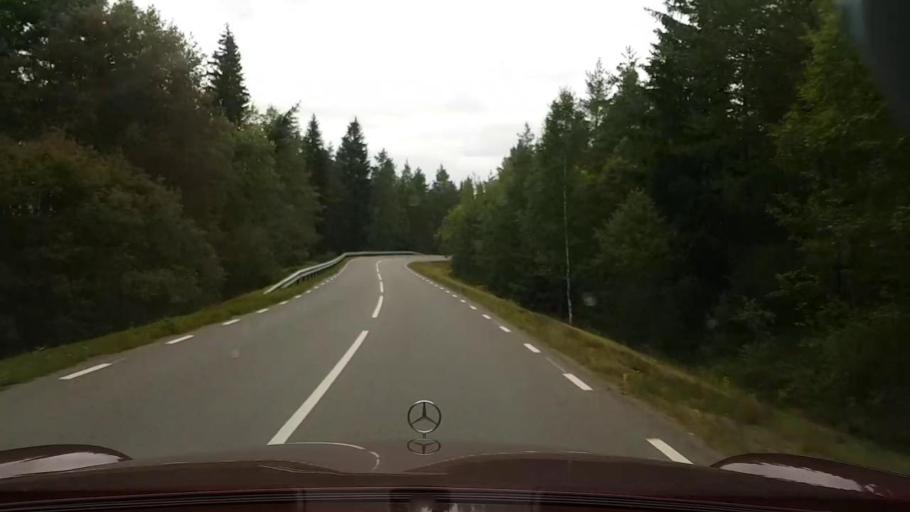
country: SE
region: Vaestra Goetaland
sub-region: Karlsborgs Kommun
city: Karlsborg
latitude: 58.7163
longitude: 14.5026
